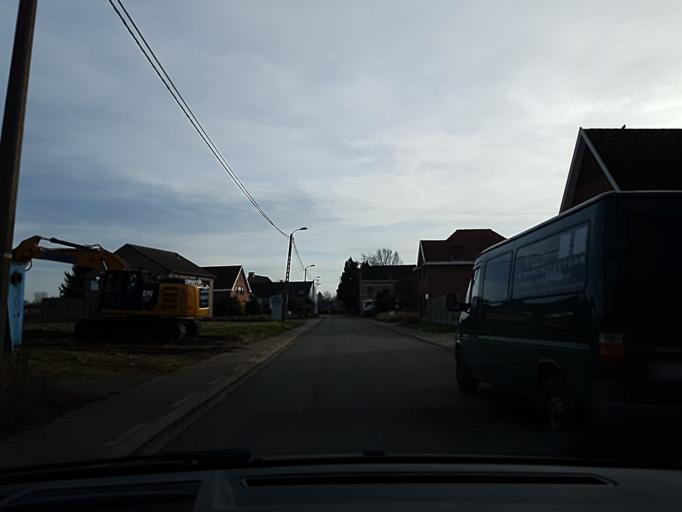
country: BE
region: Flanders
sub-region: Provincie Vlaams-Brabant
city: Haacht
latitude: 50.9607
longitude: 4.6667
